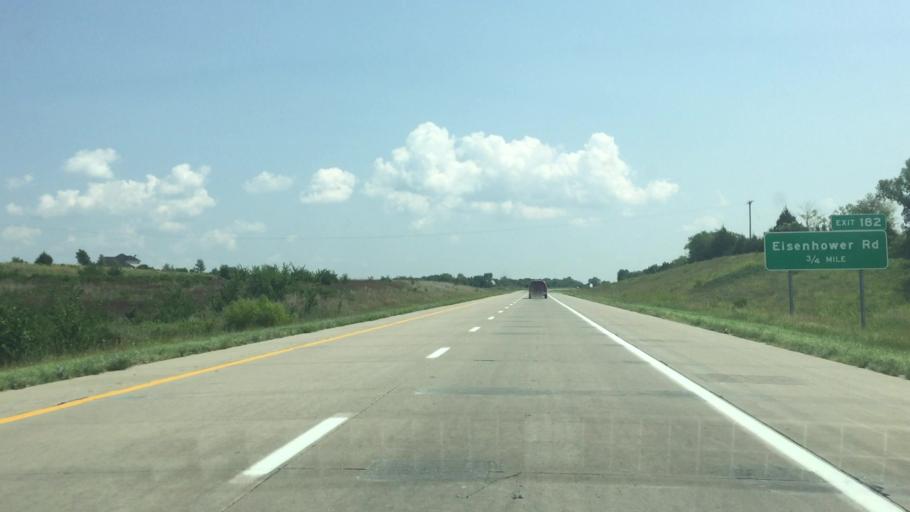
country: US
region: Kansas
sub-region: Franklin County
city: Ottawa
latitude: 38.5656
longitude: -95.3028
